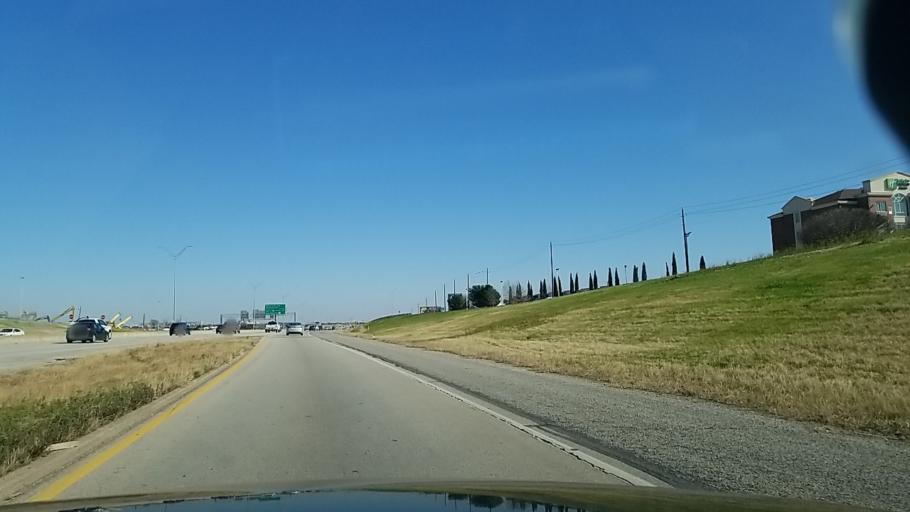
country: US
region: Texas
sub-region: Tarrant County
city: Sansom Park
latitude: 32.8143
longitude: -97.4112
